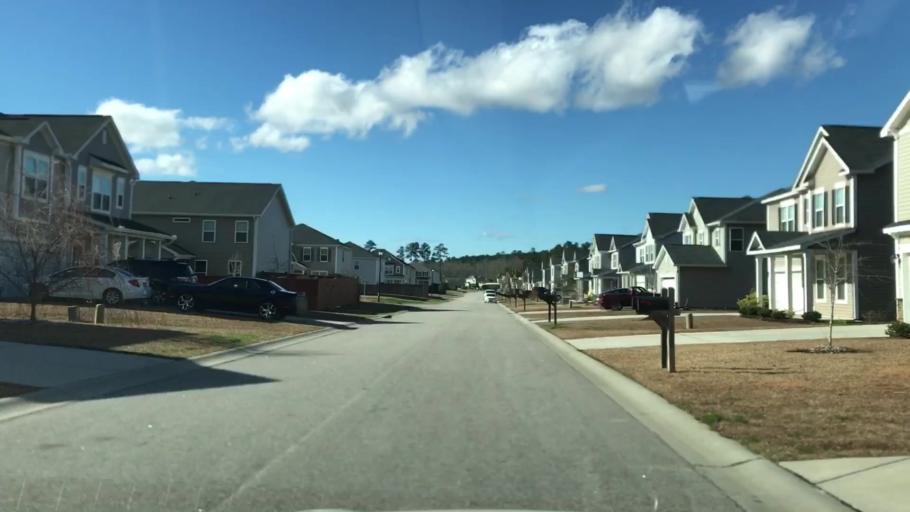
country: US
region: South Carolina
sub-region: Dorchester County
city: Summerville
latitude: 33.0894
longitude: -80.1920
